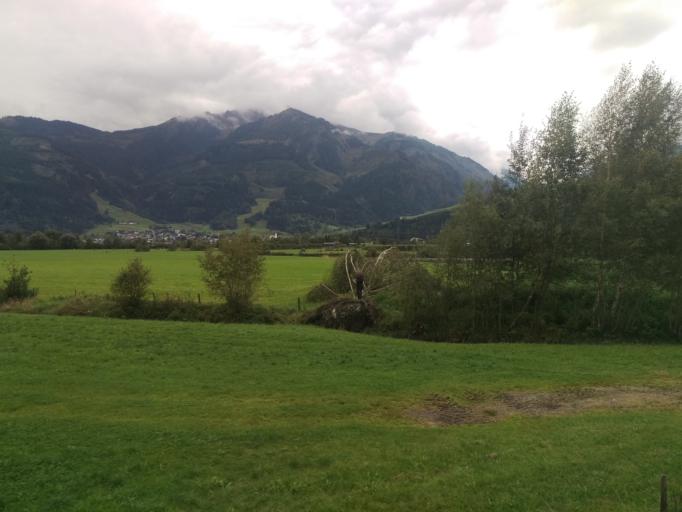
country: AT
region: Salzburg
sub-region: Politischer Bezirk Zell am See
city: Kaprun
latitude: 47.2908
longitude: 12.7511
